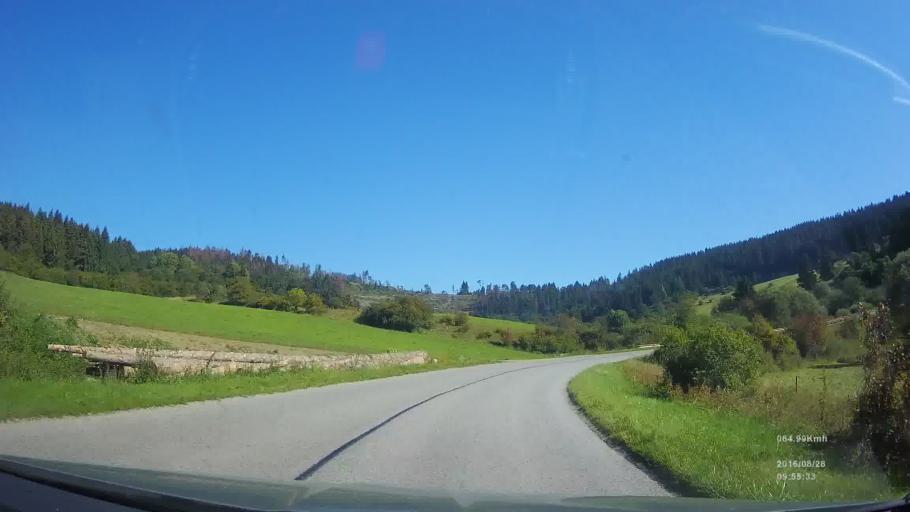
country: SK
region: Zilinsky
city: Ruzomberok
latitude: 49.1237
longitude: 19.4524
